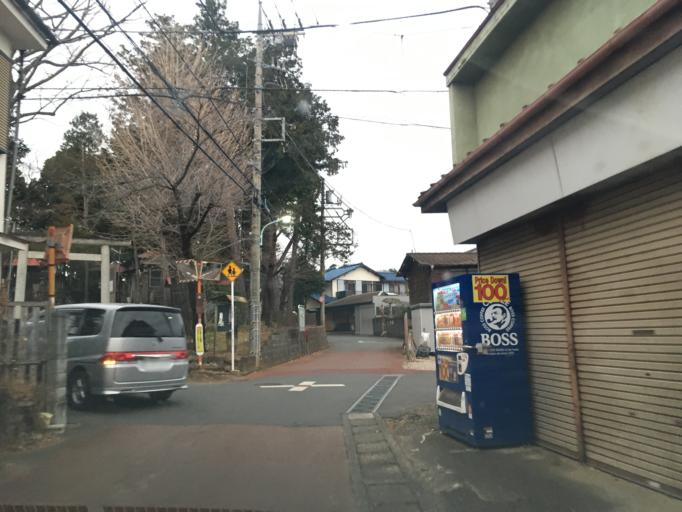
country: JP
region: Tokyo
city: Fussa
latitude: 35.7565
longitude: 139.3896
